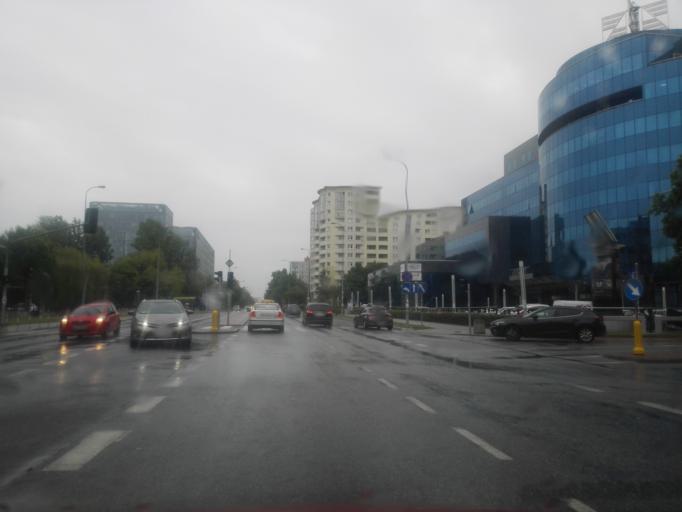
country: PL
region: Masovian Voivodeship
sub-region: Warszawa
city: Mokotow
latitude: 52.1833
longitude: 21.0058
